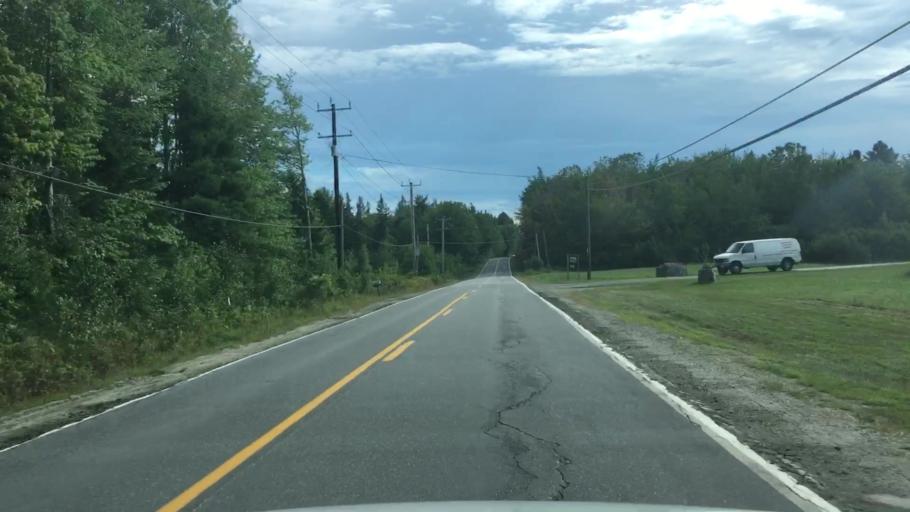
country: US
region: Maine
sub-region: Hancock County
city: Ellsworth
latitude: 44.4858
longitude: -68.4202
